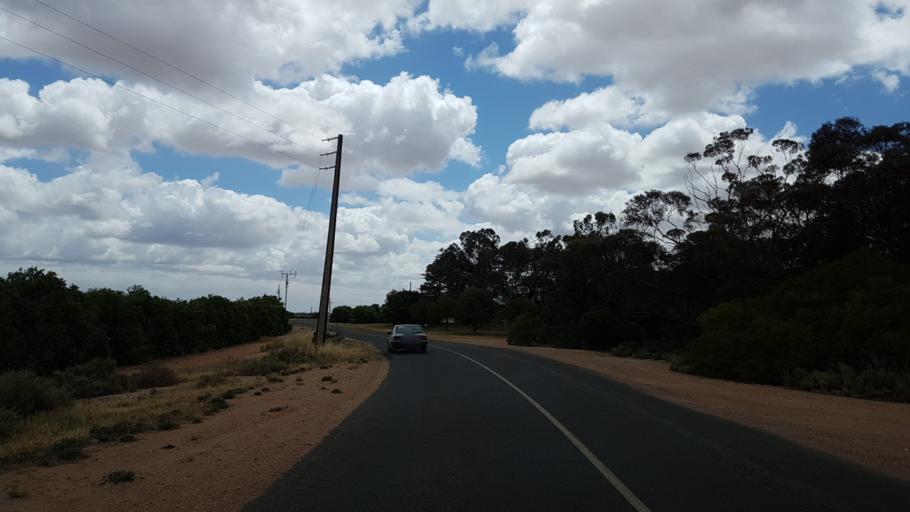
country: AU
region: South Australia
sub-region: Loxton Waikerie
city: Waikerie
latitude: -34.1782
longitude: 140.0264
